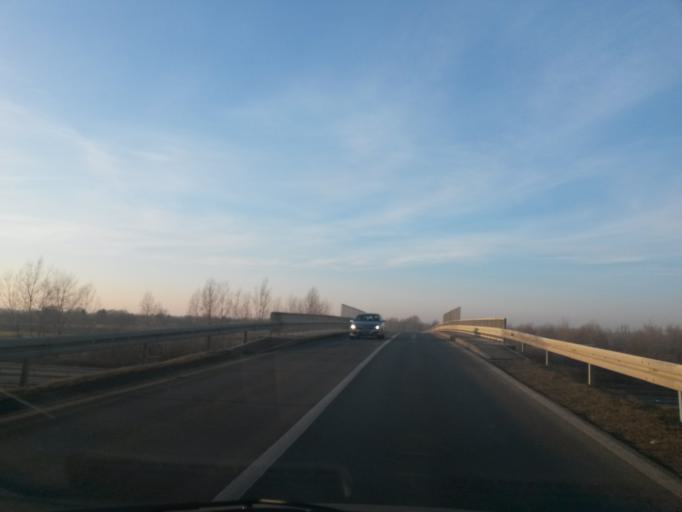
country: HR
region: Varazdinska
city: Jalzabet
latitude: 46.2943
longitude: 16.4949
